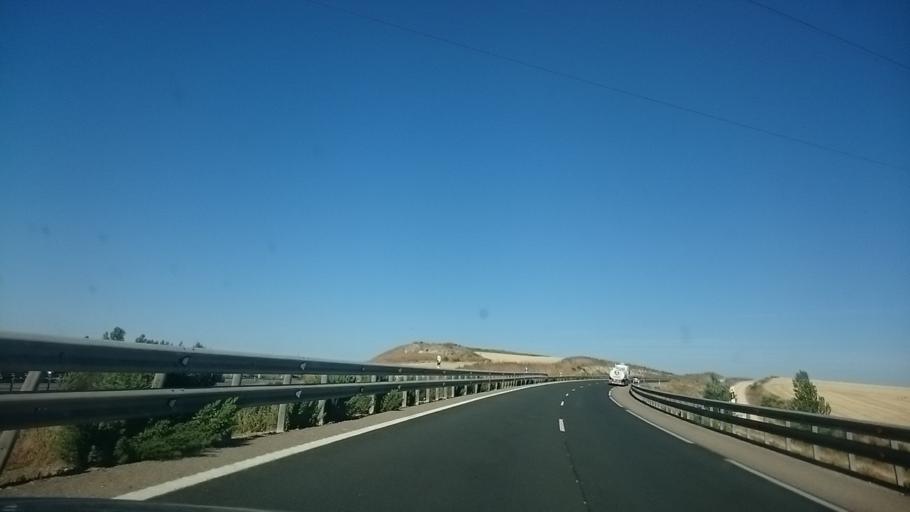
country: ES
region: Castille and Leon
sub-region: Provincia de Burgos
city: Villagonzalo-Pedernales
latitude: 42.3045
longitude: -3.7478
